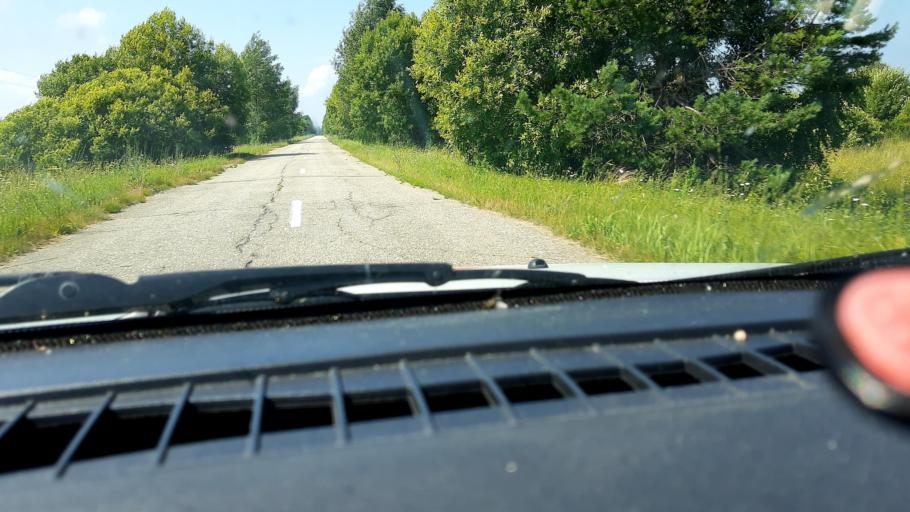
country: RU
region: Nizjnij Novgorod
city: Sharanga
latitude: 57.0660
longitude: 46.6686
